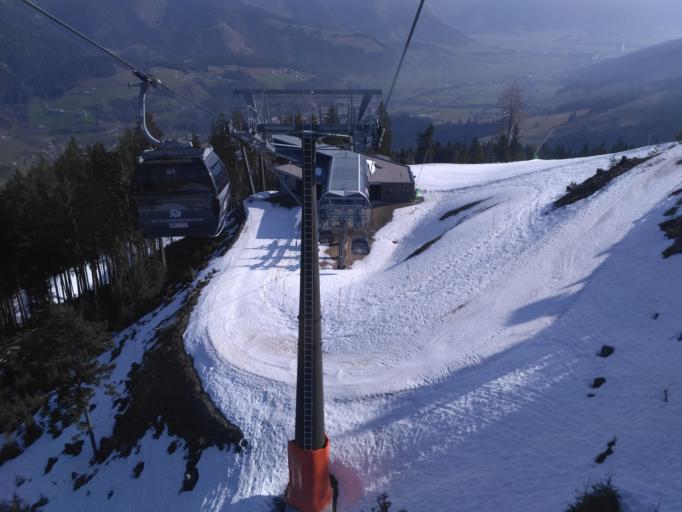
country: AT
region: Salzburg
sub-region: Politischer Bezirk Zell am See
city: Leogang
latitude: 47.4197
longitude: 12.7297
